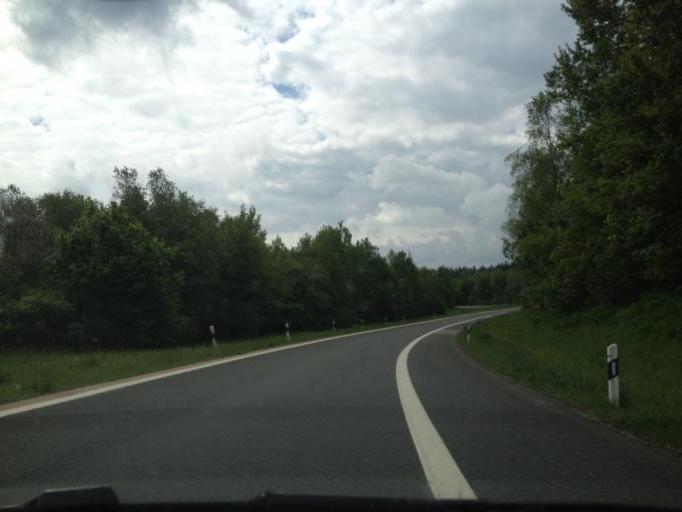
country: DE
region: Bavaria
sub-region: Regierungsbezirk Mittelfranken
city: Winkelhaid
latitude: 49.4063
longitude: 11.2950
